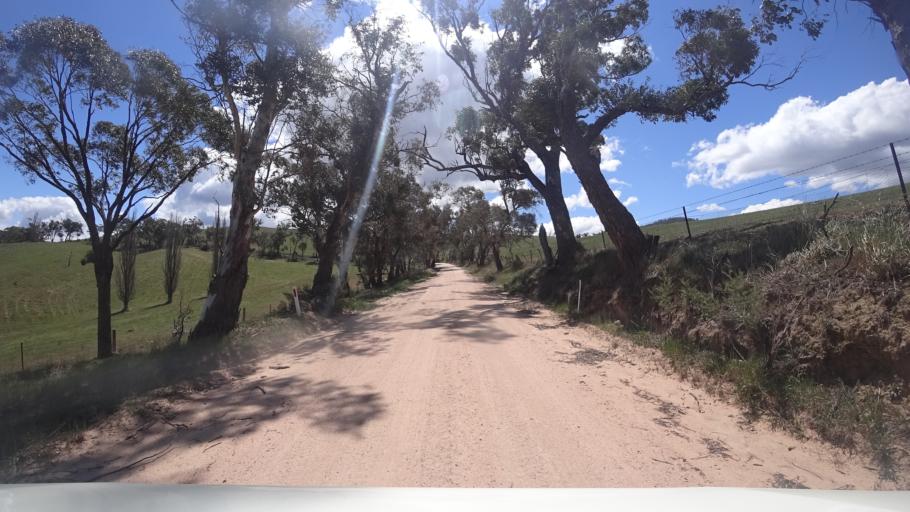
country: AU
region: New South Wales
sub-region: Oberon
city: Oberon
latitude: -33.5641
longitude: 149.9404
